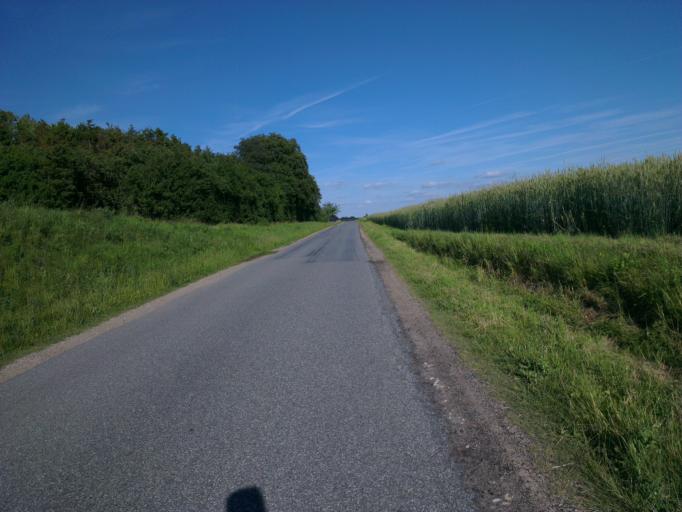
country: DK
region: Capital Region
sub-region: Frederikssund Kommune
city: Skibby
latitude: 55.7636
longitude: 11.9733
